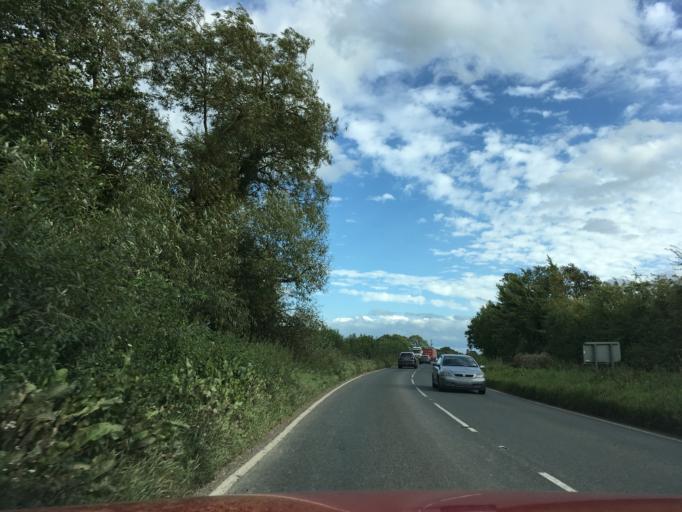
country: GB
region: England
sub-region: South Gloucestershire
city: Charfield
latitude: 51.6296
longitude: -2.4218
